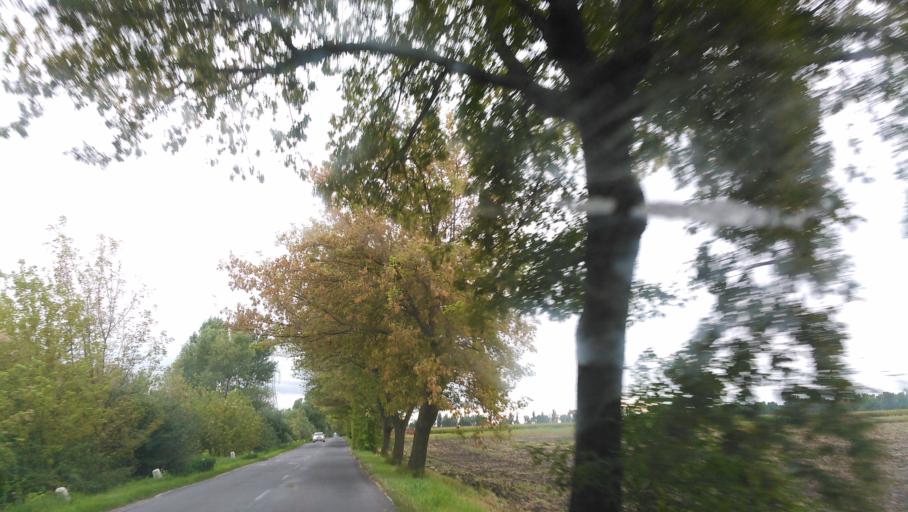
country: SK
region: Trnavsky
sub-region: Okres Dunajska Streda
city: Velky Meder
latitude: 47.9021
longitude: 17.7872
